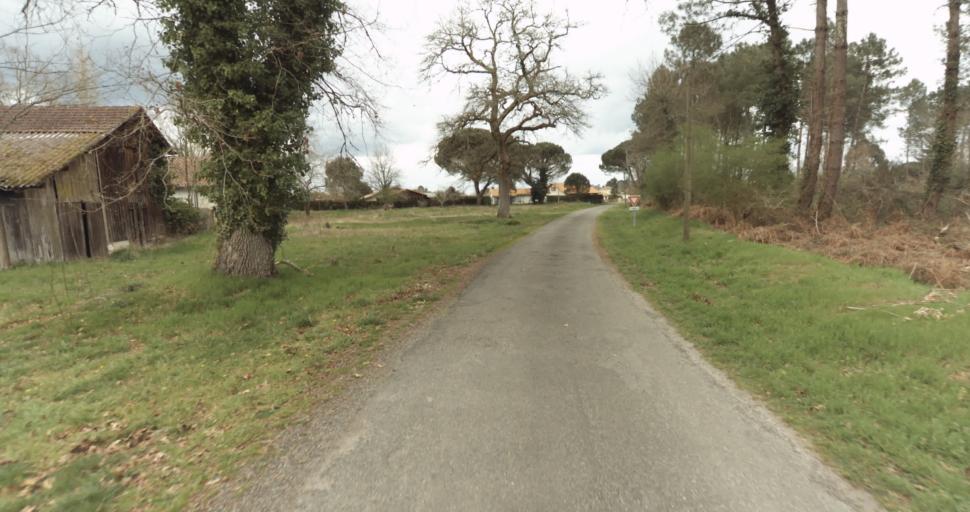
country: FR
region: Aquitaine
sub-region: Departement des Landes
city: Sarbazan
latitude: 44.0172
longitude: -0.3155
